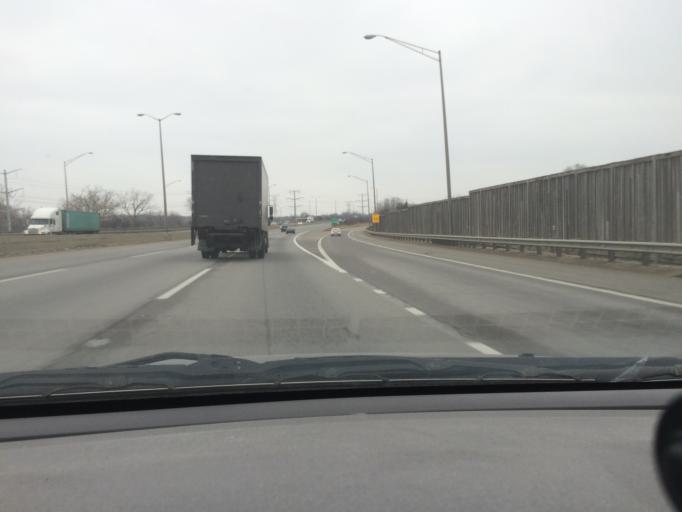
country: US
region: Illinois
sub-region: DuPage County
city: Glen Ellyn
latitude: 41.8533
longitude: -88.0391
